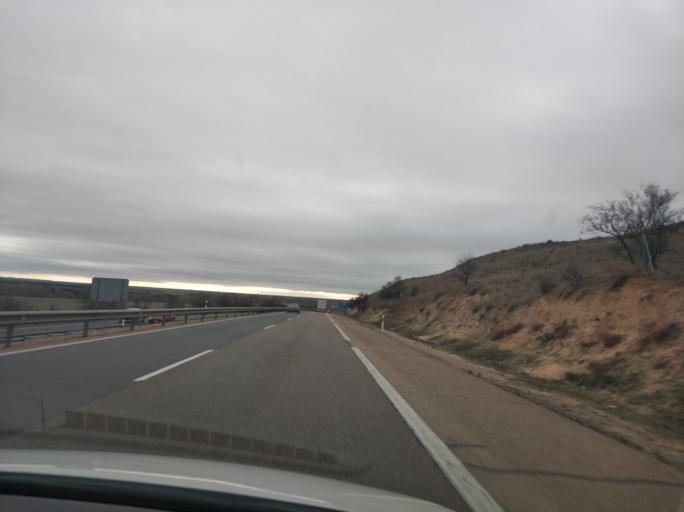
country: ES
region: Castille and Leon
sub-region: Provincia de Valladolid
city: Simancas
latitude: 41.5836
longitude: -4.8368
